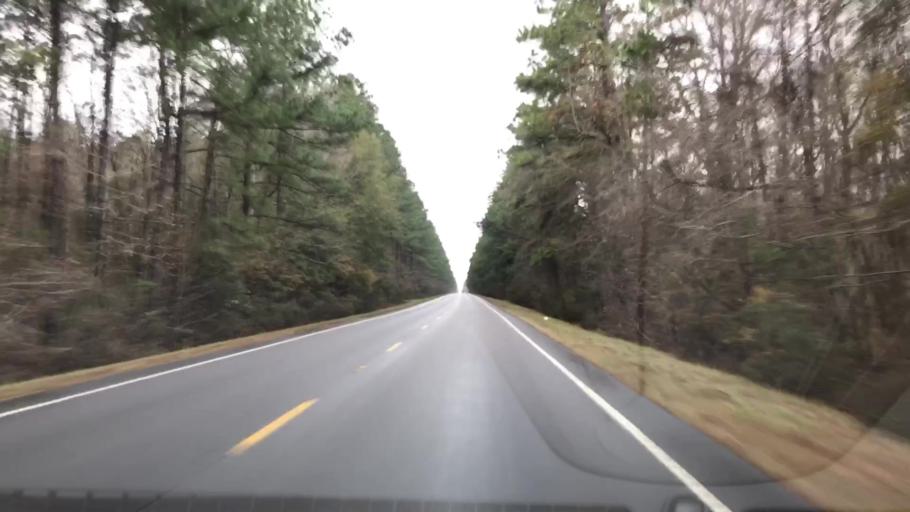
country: US
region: South Carolina
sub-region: Berkeley County
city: Saint Stephen
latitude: 33.2901
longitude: -79.7967
